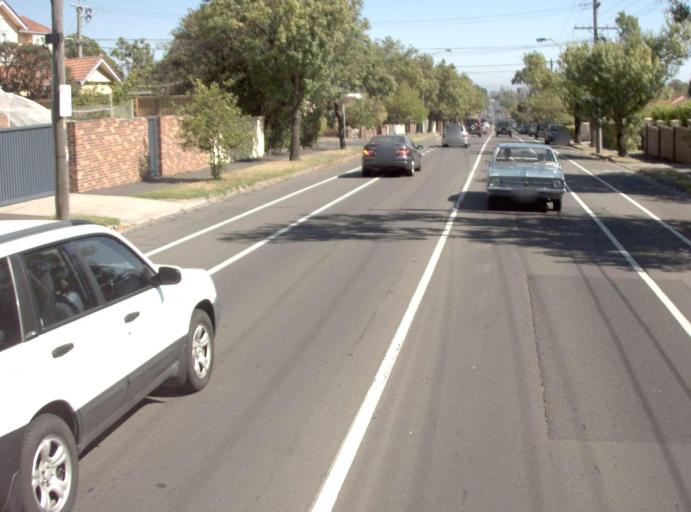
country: AU
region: Victoria
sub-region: Bayside
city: Hampton
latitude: -37.9236
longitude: 145.0051
